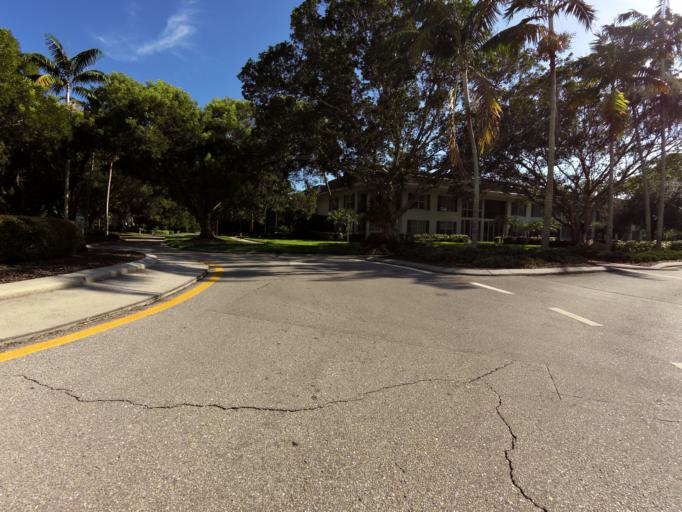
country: US
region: Florida
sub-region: Collier County
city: Naples
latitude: 26.1626
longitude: -81.8066
